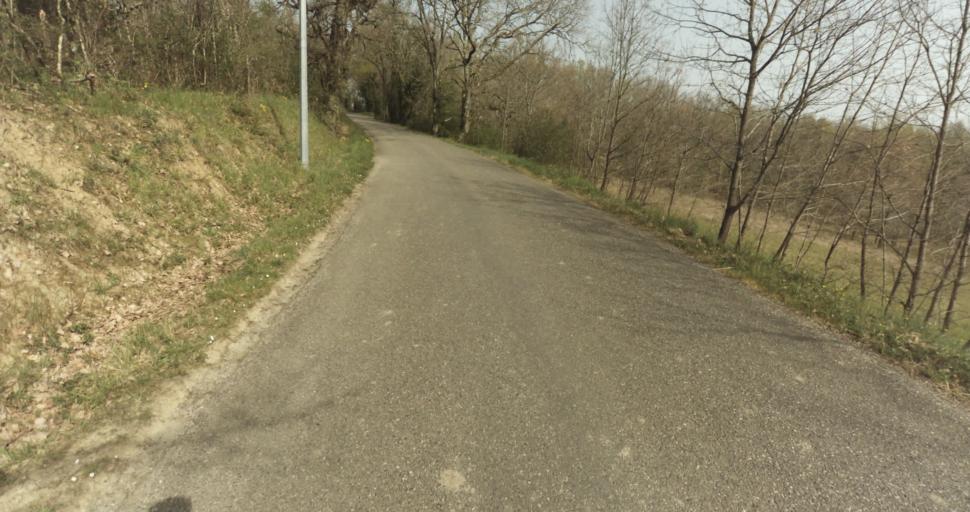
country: FR
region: Midi-Pyrenees
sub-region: Departement du Tarn-et-Garonne
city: Moissac
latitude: 44.1317
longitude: 1.0970
